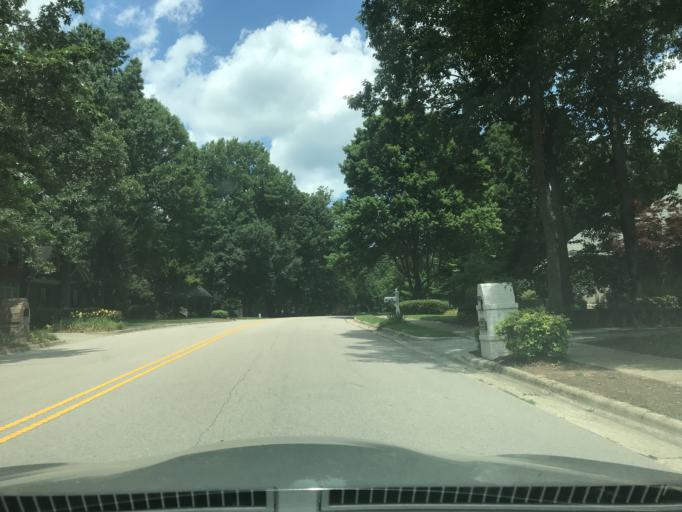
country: US
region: North Carolina
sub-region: Wake County
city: West Raleigh
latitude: 35.8895
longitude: -78.6050
